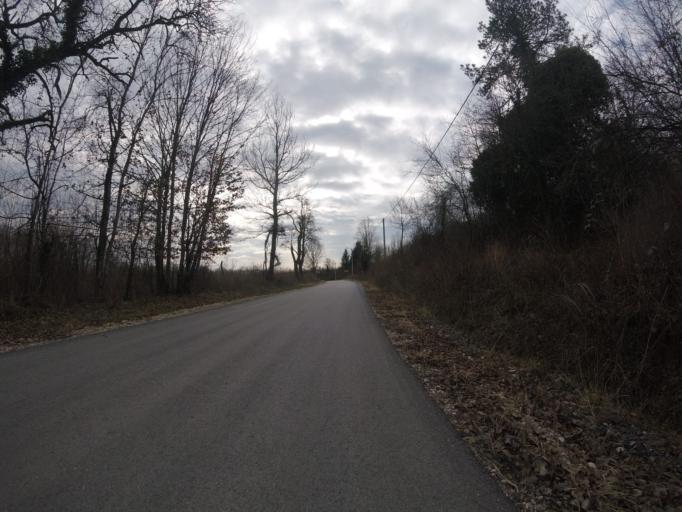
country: HR
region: Sisacko-Moslavacka
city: Glina
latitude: 45.4364
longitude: 16.0769
